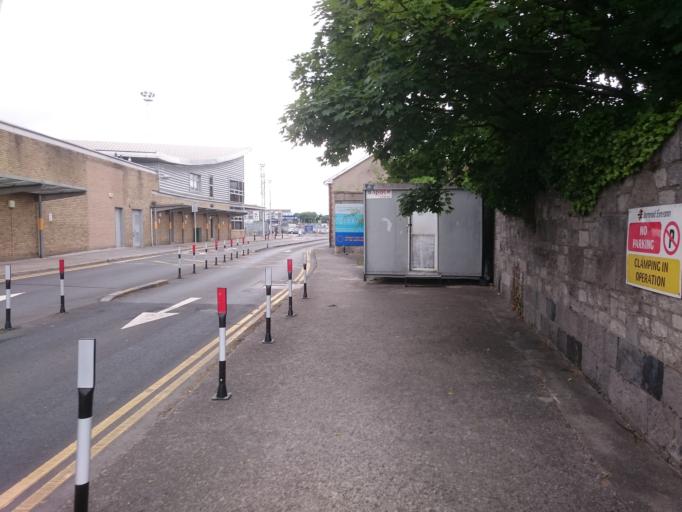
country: IE
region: Leinster
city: Rialto
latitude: 53.3467
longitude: -6.2960
